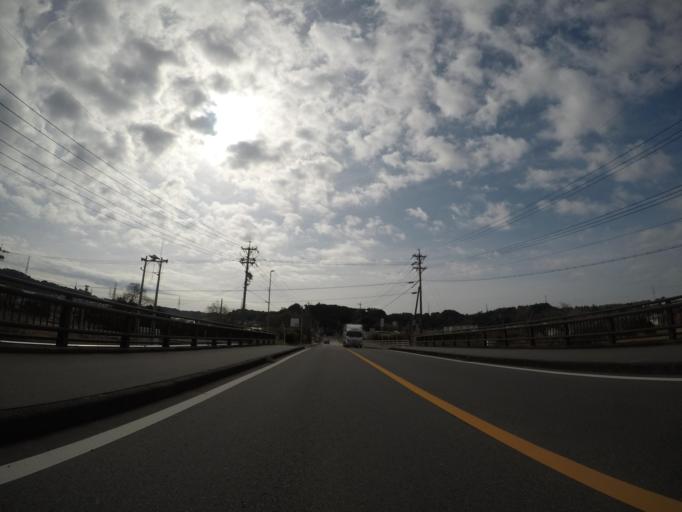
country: JP
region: Shizuoka
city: Hamakita
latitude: 34.8093
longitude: 137.6860
